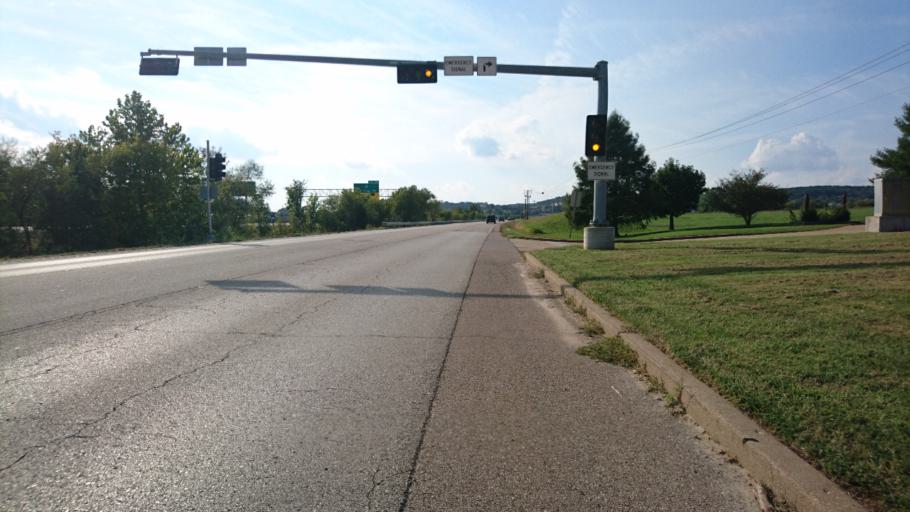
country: US
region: Missouri
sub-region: Saint Louis County
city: Eureka
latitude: 38.5050
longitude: -90.6685
